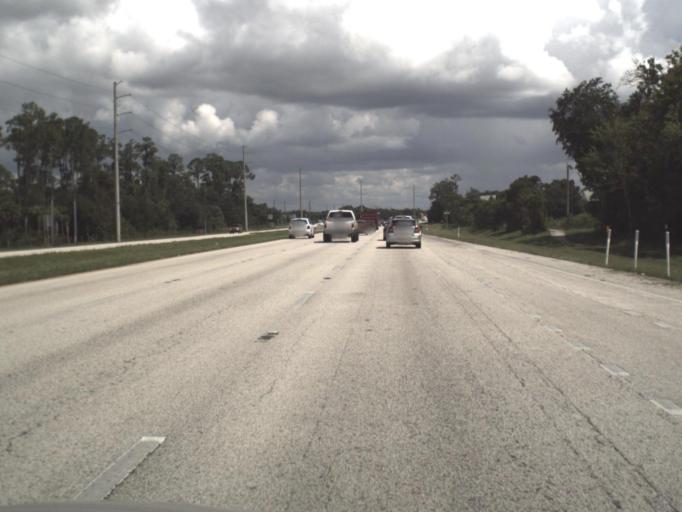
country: US
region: Florida
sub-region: Manatee County
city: Samoset
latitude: 27.4459
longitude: -82.4805
